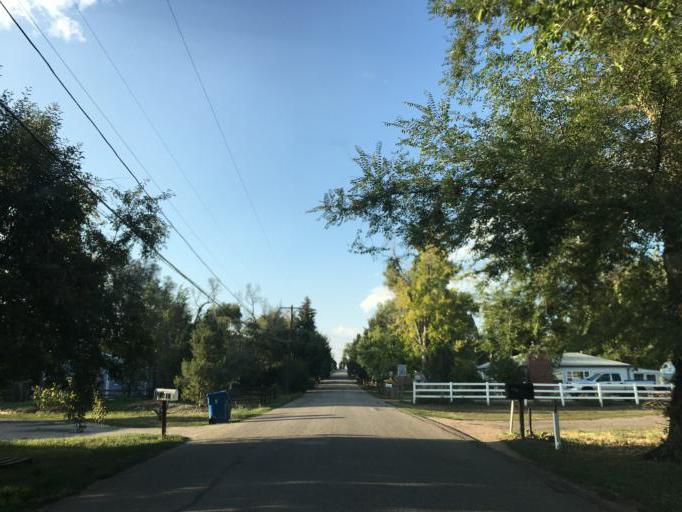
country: US
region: Colorado
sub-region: Jefferson County
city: Applewood
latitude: 39.7908
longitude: -105.1568
